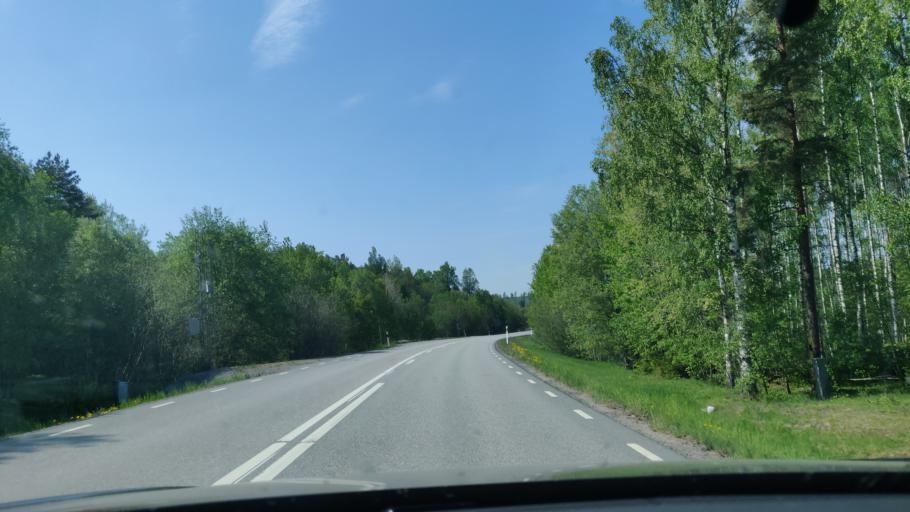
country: SE
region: Uppsala
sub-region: Heby Kommun
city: OEstervala
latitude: 60.1449
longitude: 17.2038
